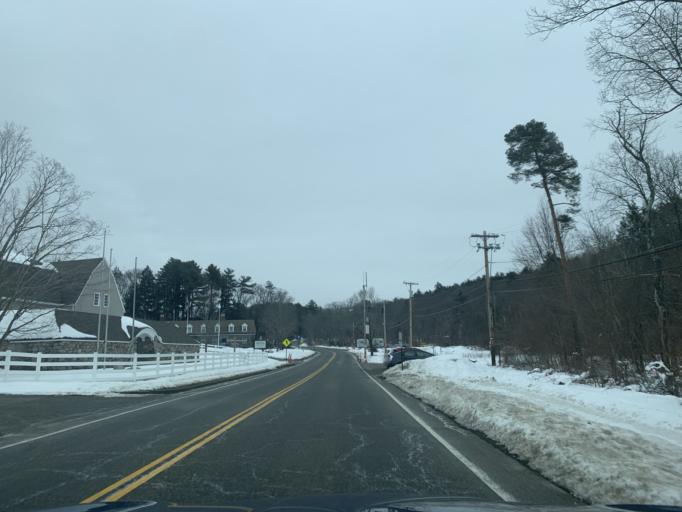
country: US
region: Massachusetts
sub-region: Norfolk County
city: Milton
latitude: 42.2133
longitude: -71.0939
